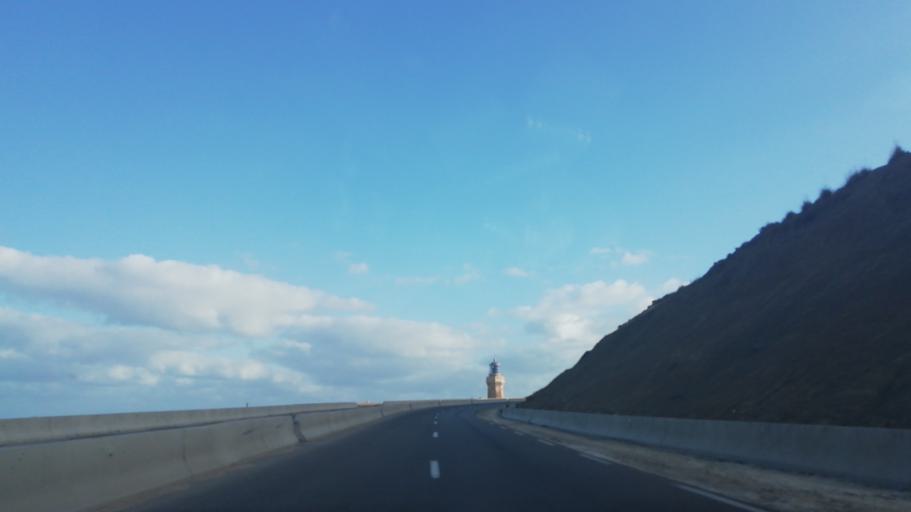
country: DZ
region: Mostaganem
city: Mostaganem
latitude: 36.1106
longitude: 0.2257
